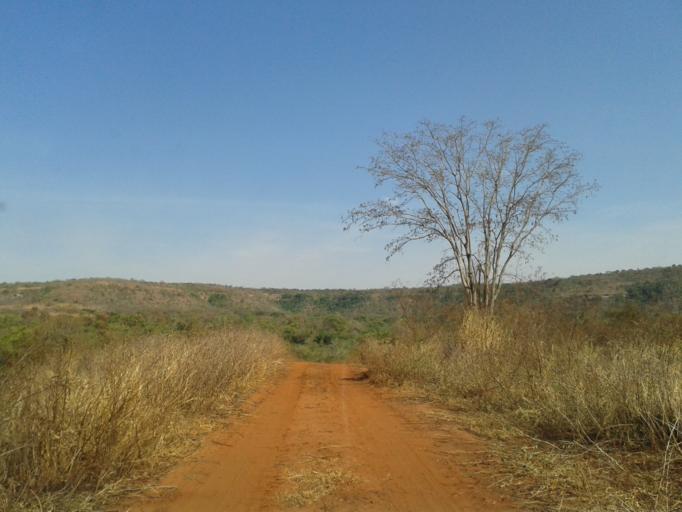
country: BR
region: Minas Gerais
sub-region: Santa Vitoria
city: Santa Vitoria
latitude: -19.2072
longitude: -50.0337
